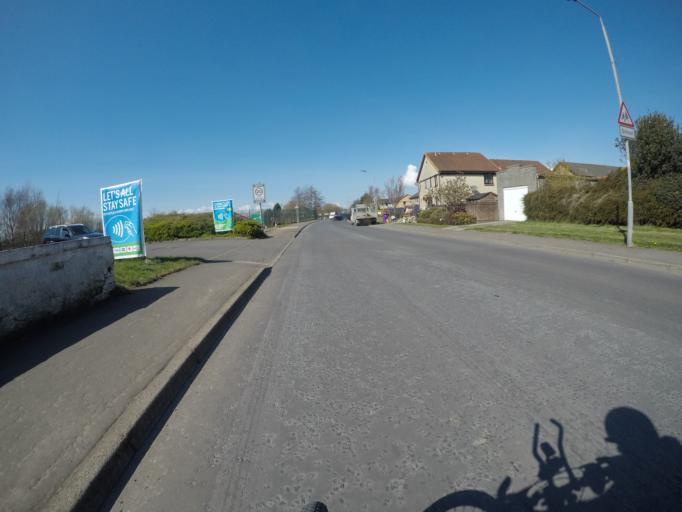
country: GB
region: Scotland
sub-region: North Ayrshire
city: Irvine
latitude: 55.6190
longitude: -4.6566
